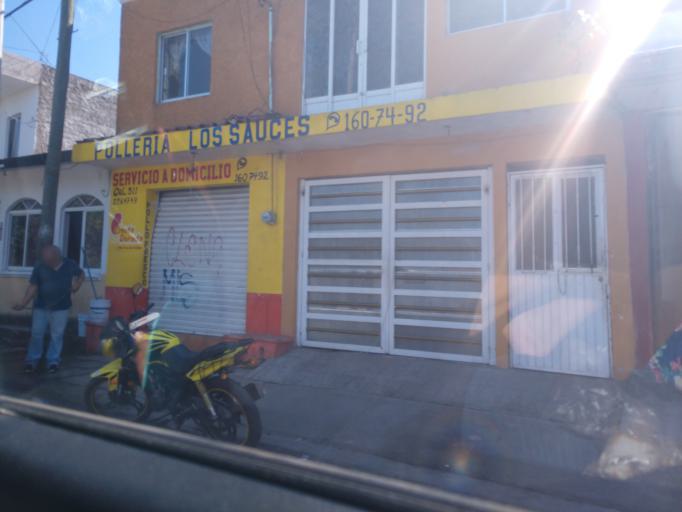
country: MX
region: Nayarit
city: Xalisco
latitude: 21.4699
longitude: -104.8714
